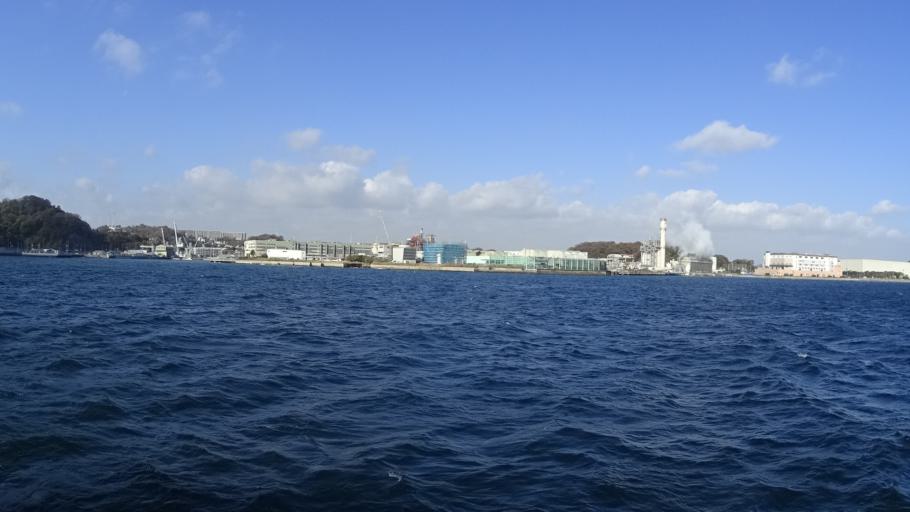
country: JP
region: Kanagawa
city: Yokosuka
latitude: 35.3062
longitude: 139.6473
